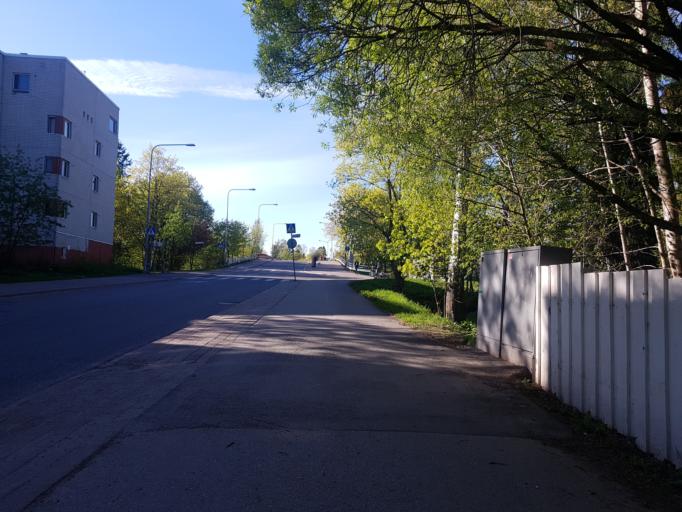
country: FI
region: Uusimaa
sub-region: Helsinki
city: Vantaa
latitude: 60.2608
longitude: 25.0291
